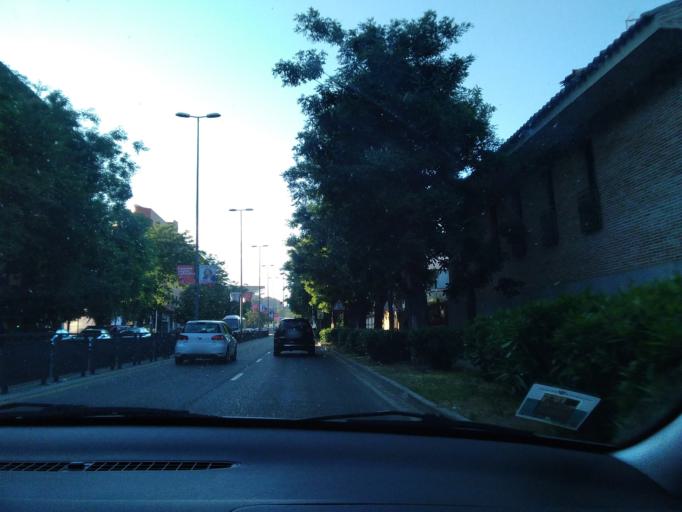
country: ES
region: Castille-La Mancha
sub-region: Province of Toledo
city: Toledo
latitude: 39.8691
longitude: -4.0312
